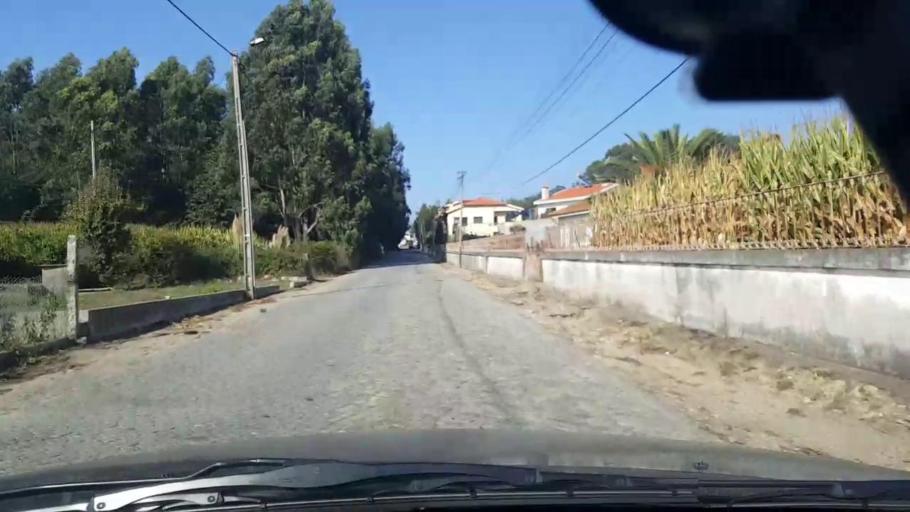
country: PT
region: Porto
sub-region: Matosinhos
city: Lavra
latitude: 41.2669
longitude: -8.6823
